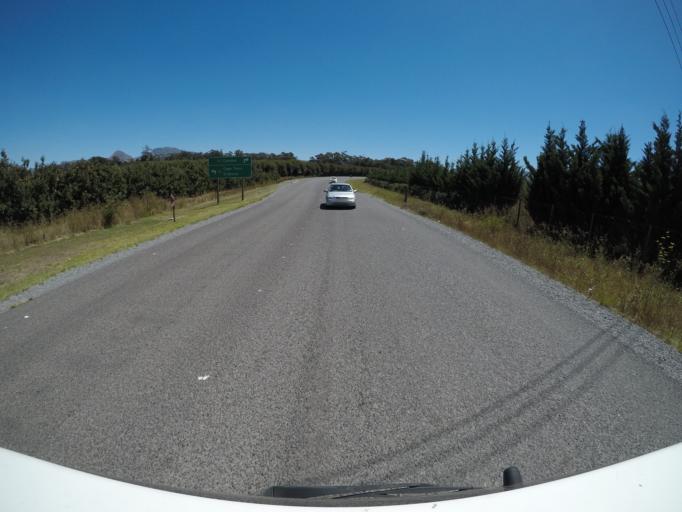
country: ZA
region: Western Cape
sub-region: Overberg District Municipality
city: Grabouw
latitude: -34.1680
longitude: 19.0363
